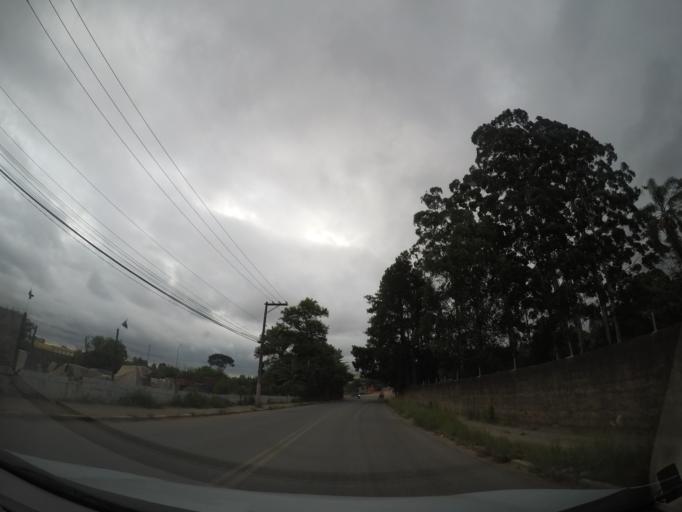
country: BR
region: Sao Paulo
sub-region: Guarulhos
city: Guarulhos
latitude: -23.4073
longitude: -46.4408
